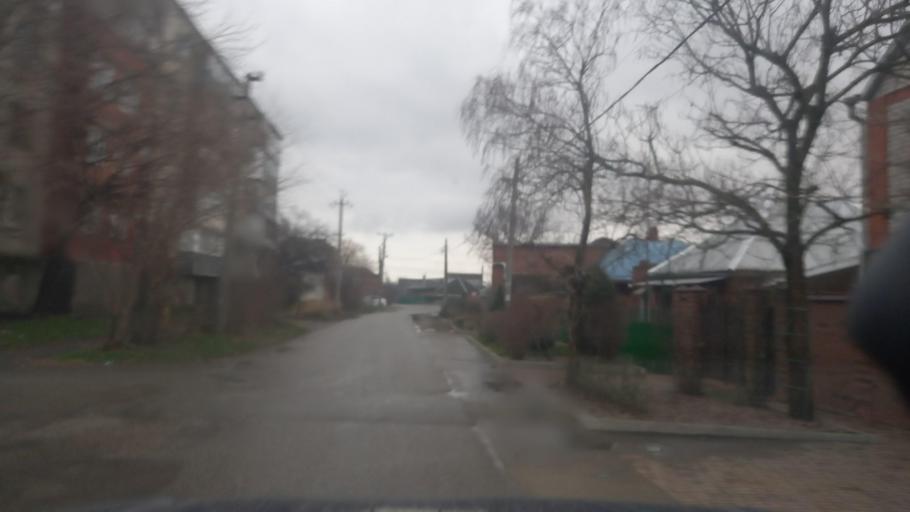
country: RU
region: Adygeya
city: Yablonovskiy
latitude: 44.9808
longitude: 38.9341
